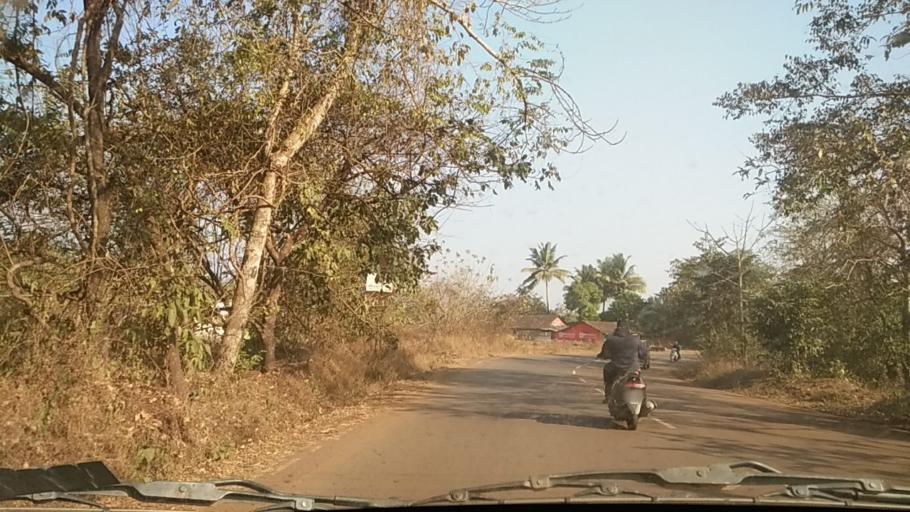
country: IN
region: Goa
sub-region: South Goa
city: Sanvordem
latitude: 15.3097
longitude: 74.1383
